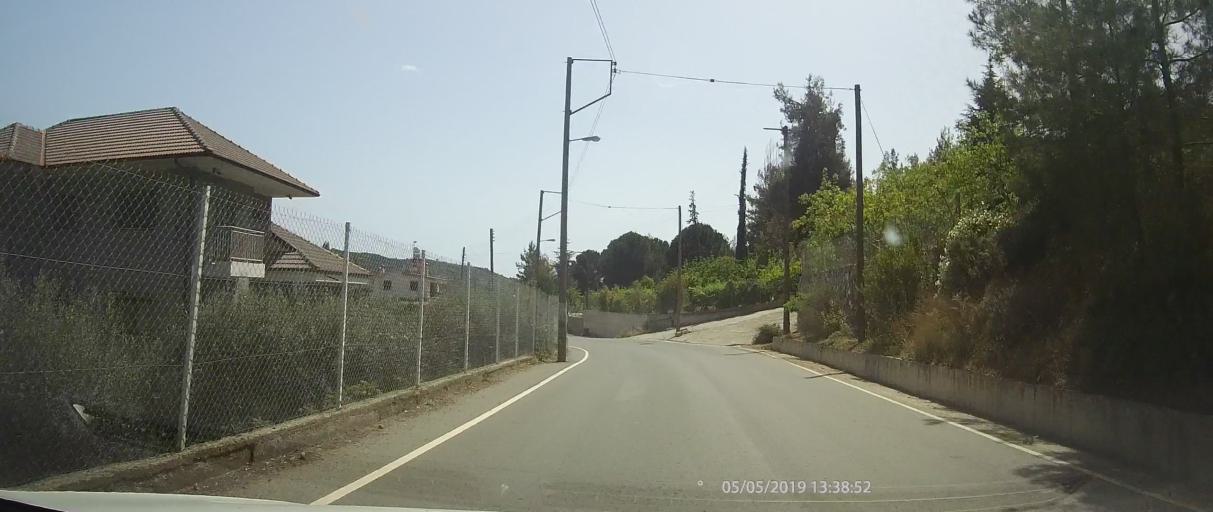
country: CY
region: Limassol
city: Pachna
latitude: 34.8734
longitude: 32.8328
